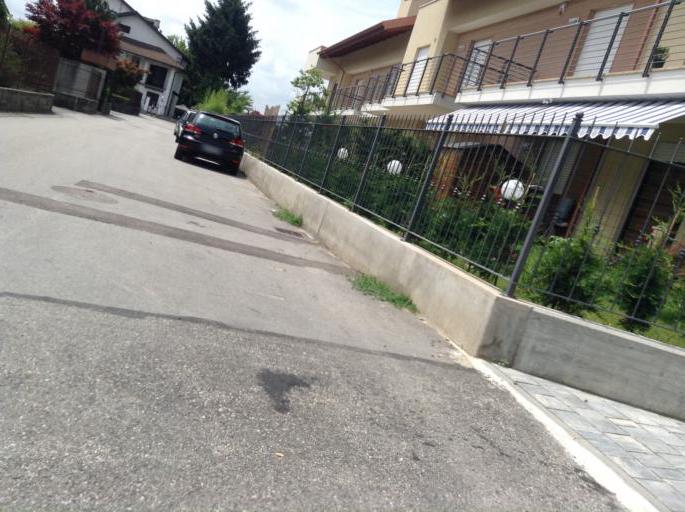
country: IT
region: Piedmont
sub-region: Provincia di Torino
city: Carignano
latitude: 44.9154
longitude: 7.6760
